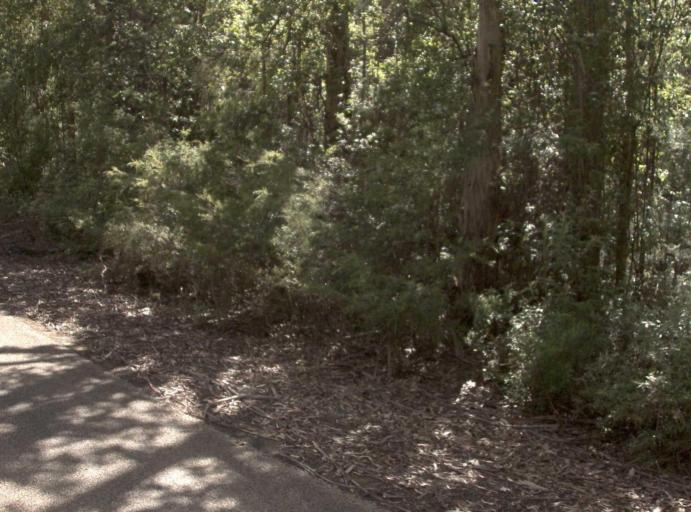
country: AU
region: Victoria
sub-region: East Gippsland
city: Lakes Entrance
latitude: -37.4553
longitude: 148.1226
